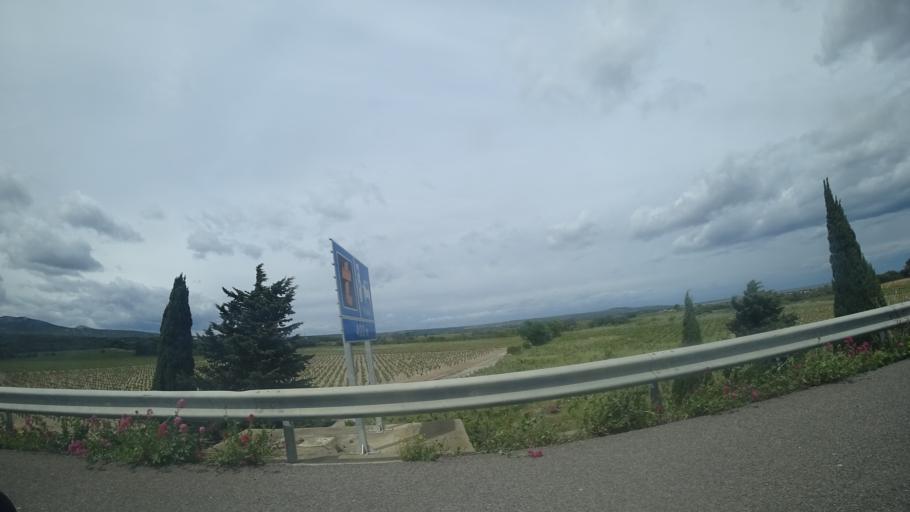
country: FR
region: Languedoc-Roussillon
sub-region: Departement de l'Aude
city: Leucate
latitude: 42.9387
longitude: 2.9770
